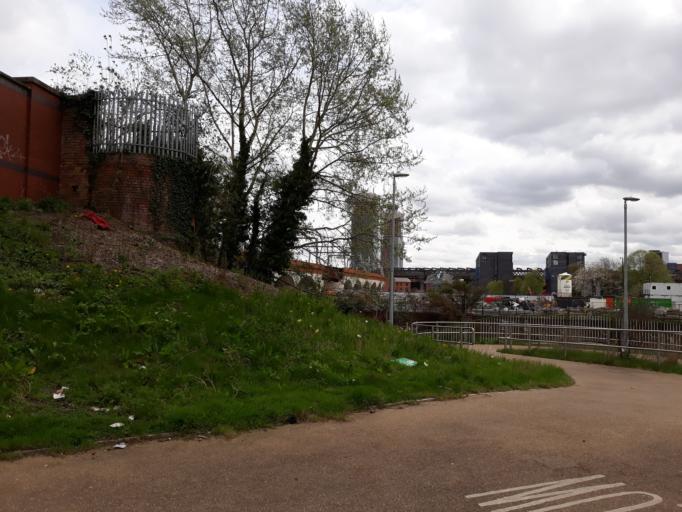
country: GB
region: England
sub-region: Manchester
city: Hulme
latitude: 53.4780
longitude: -2.2610
